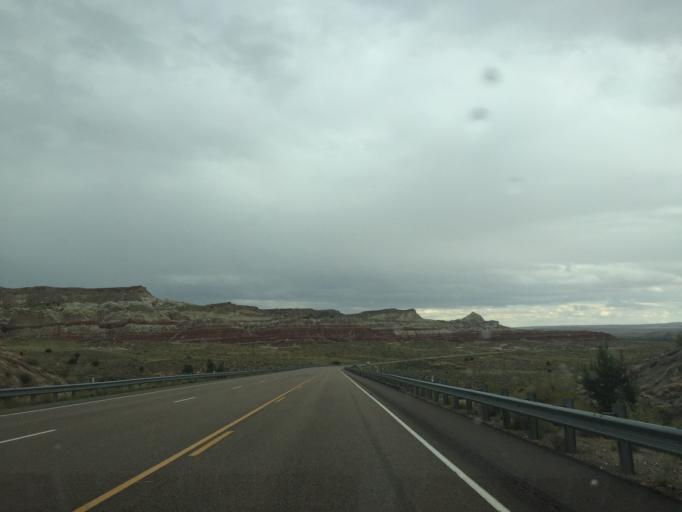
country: US
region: Arizona
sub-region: Coconino County
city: Page
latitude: 37.1278
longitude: -111.9597
